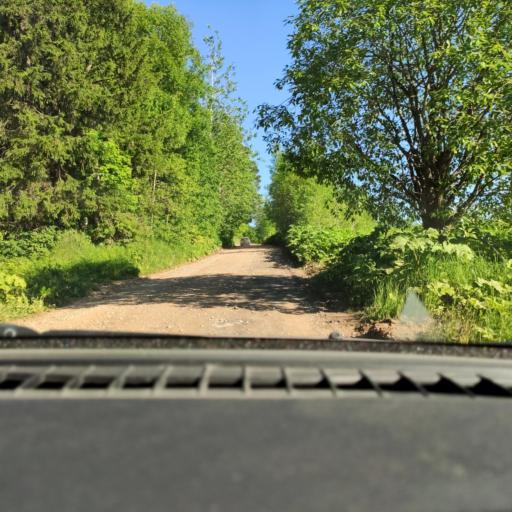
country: RU
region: Perm
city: Overyata
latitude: 58.1260
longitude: 55.8765
